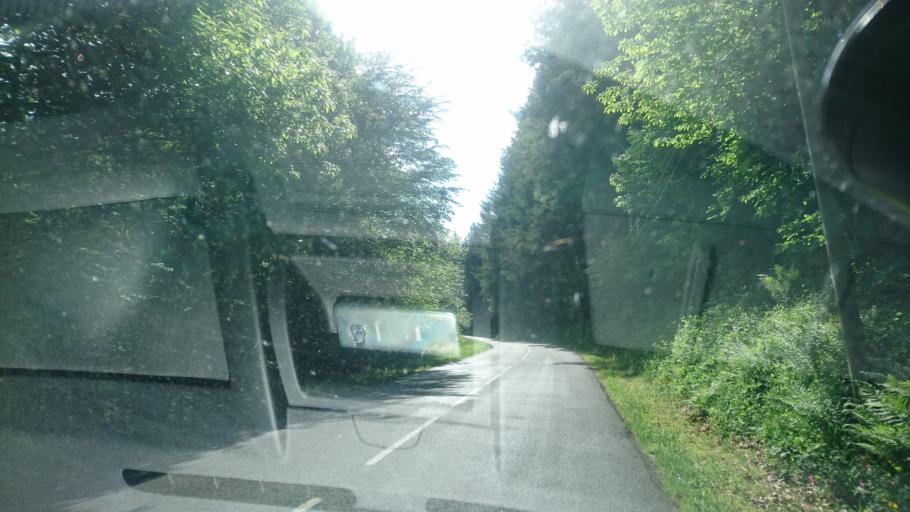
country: FR
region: Limousin
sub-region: Departement de la Haute-Vienne
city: Peyrat-le-Chateau
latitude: 45.8118
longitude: 1.8104
